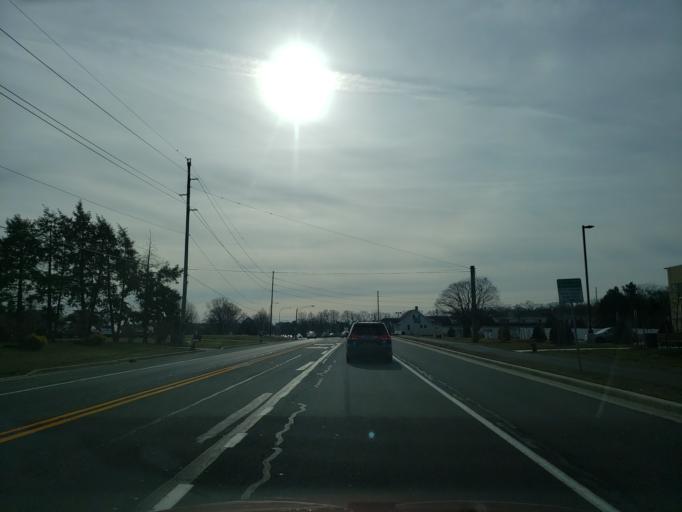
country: US
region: Delaware
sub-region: Kent County
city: Dover
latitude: 39.1775
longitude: -75.5552
